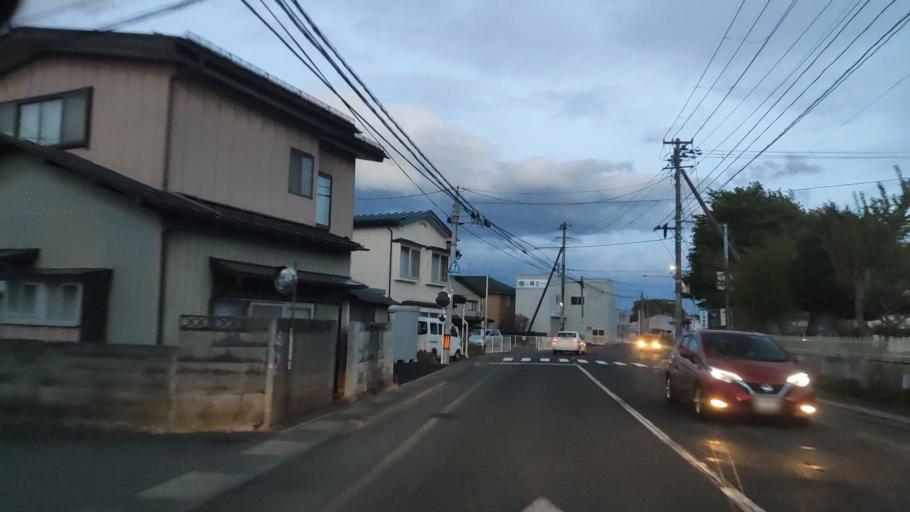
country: JP
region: Iwate
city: Morioka-shi
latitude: 39.7195
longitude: 141.1213
